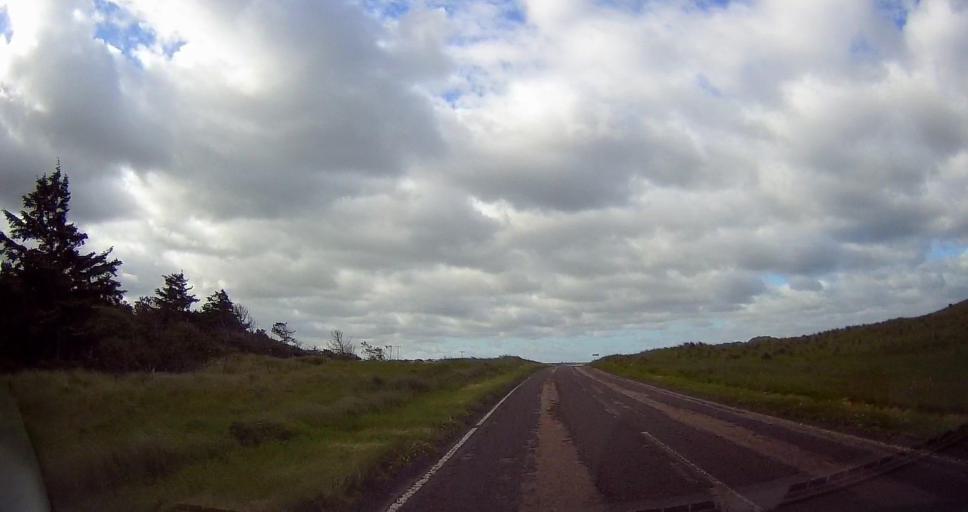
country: GB
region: Scotland
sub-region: Highland
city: Thurso
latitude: 58.6113
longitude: -3.3432
